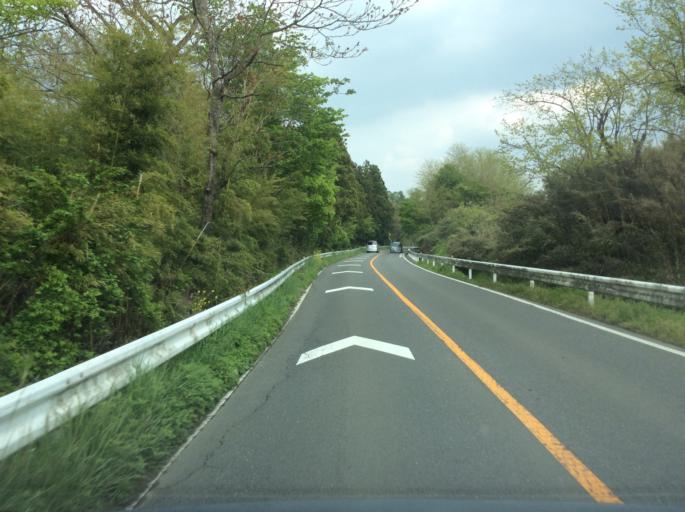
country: JP
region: Fukushima
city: Koriyama
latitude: 37.4226
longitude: 140.4204
